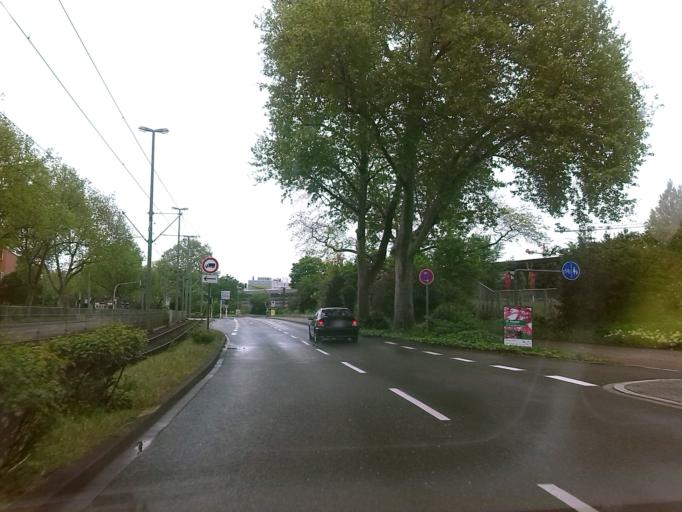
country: DE
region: Rheinland-Pfalz
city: Ludwigshafen am Rhein
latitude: 49.5000
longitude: 8.4246
